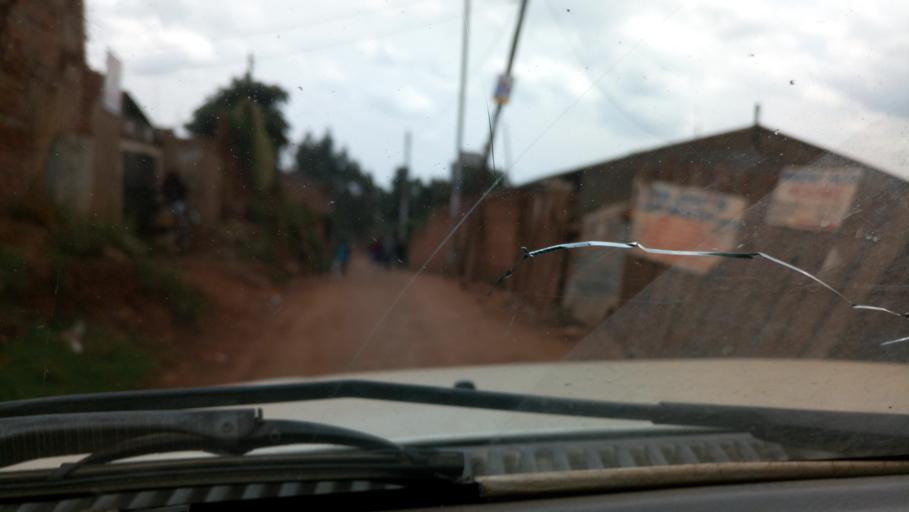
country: KE
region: Nairobi Area
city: Nairobi
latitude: -1.2693
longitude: 36.7490
